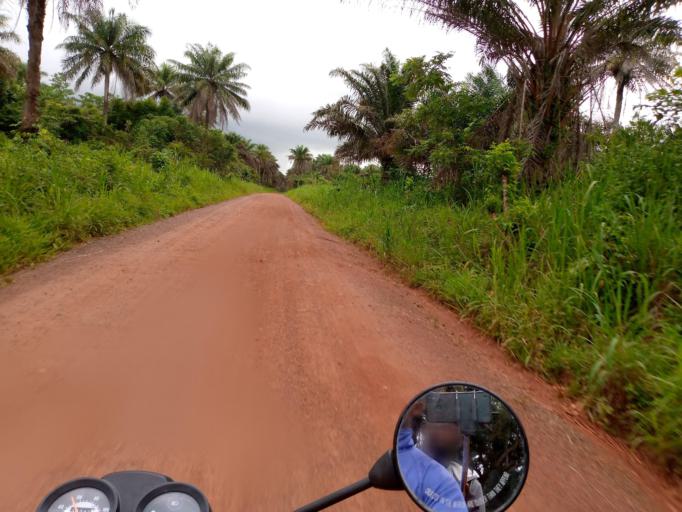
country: SL
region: Northern Province
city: Port Loko
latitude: 8.8771
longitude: -12.7256
